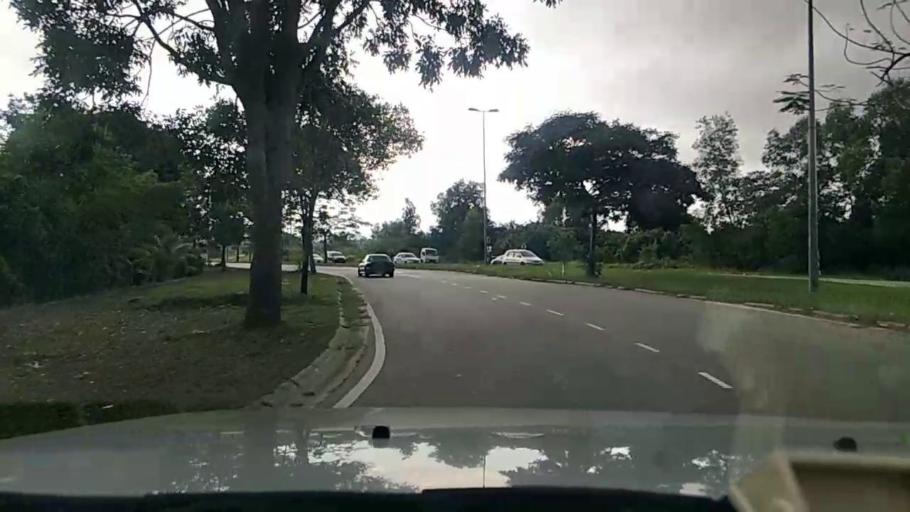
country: MY
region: Putrajaya
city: Putrajaya
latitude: 2.9360
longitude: 101.6188
